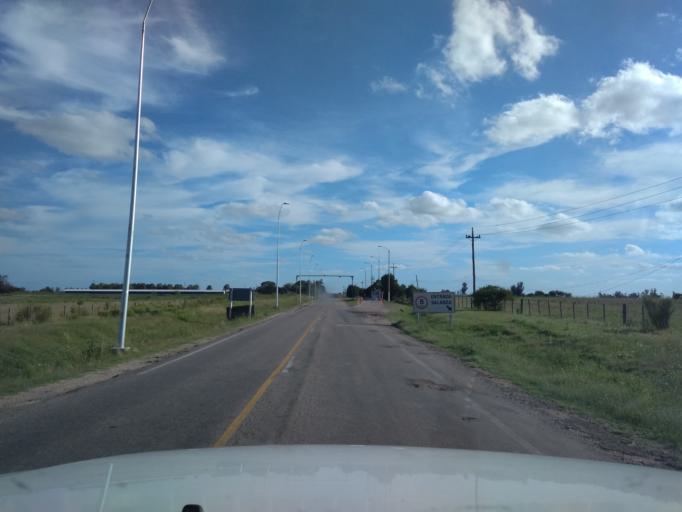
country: UY
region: Canelones
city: San Ramon
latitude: -34.2434
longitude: -55.9254
